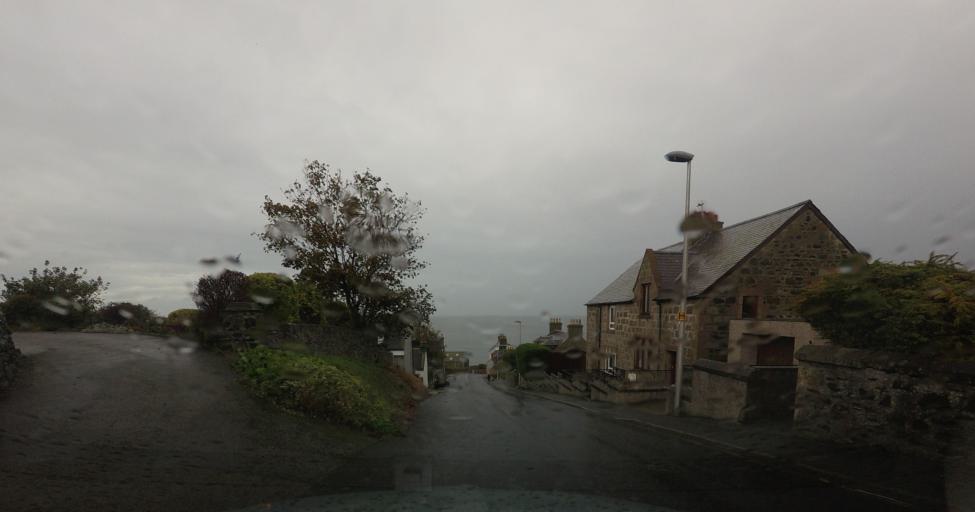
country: GB
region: Scotland
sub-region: Aberdeenshire
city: Macduff
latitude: 57.6679
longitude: -2.4996
